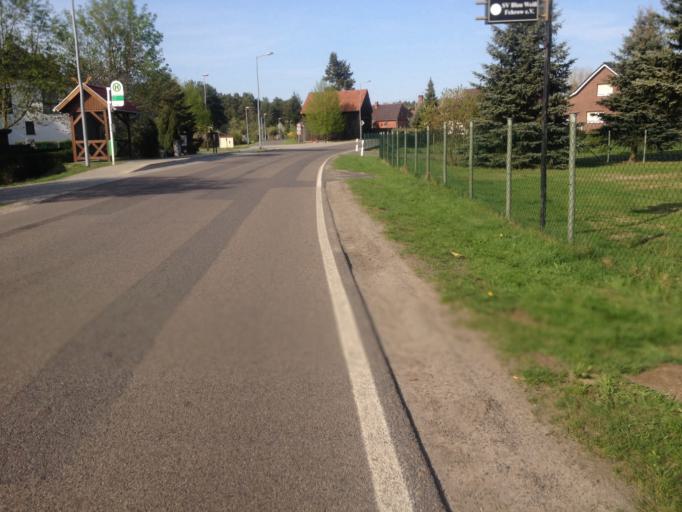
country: DE
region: Brandenburg
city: Briesen
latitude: 51.8552
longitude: 14.2499
